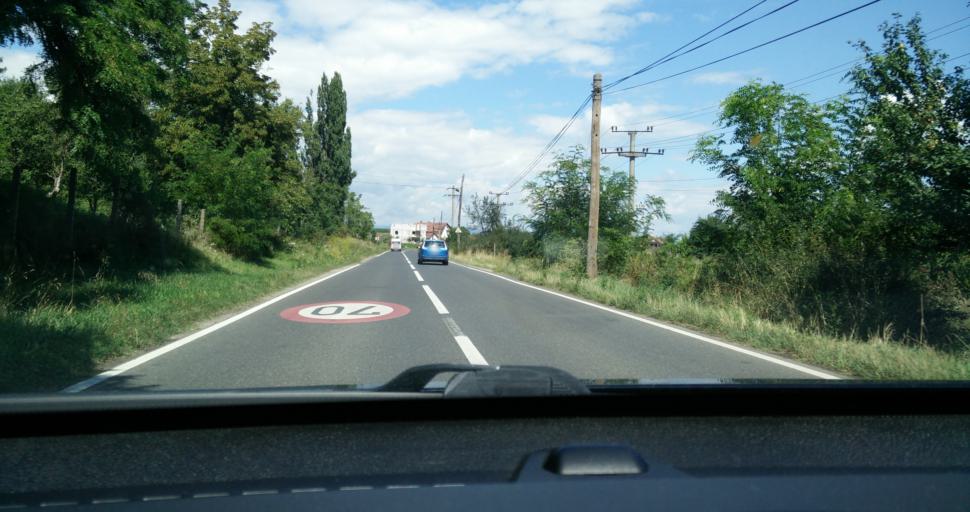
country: RO
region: Alba
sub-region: Municipiul Sebes
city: Petresti
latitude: 45.9093
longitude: 23.5546
